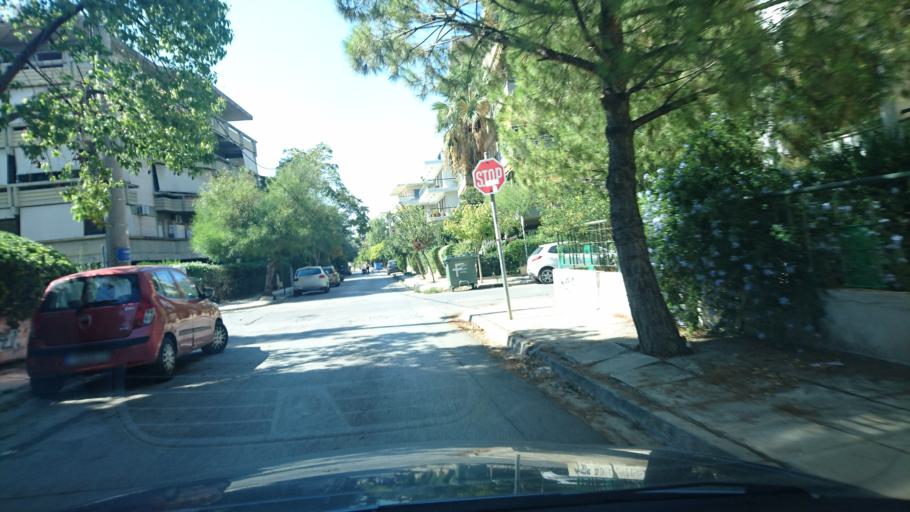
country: GR
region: Attica
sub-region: Nomarchia Athinas
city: Khalandrion
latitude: 38.0154
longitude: 23.8069
